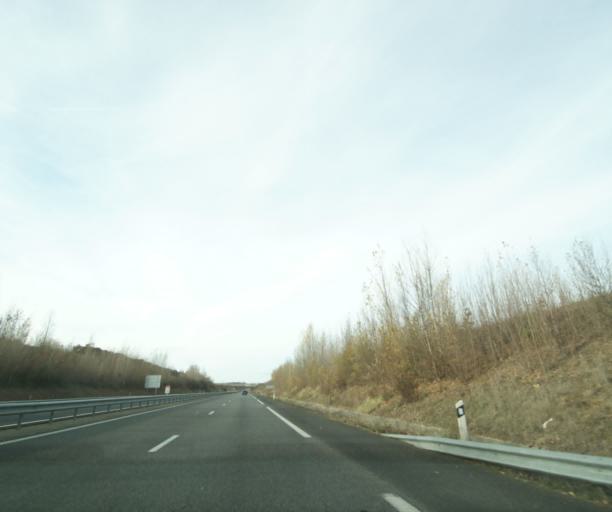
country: FR
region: Midi-Pyrenees
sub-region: Departement du Gers
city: Pujaudran
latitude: 43.6022
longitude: 1.0839
